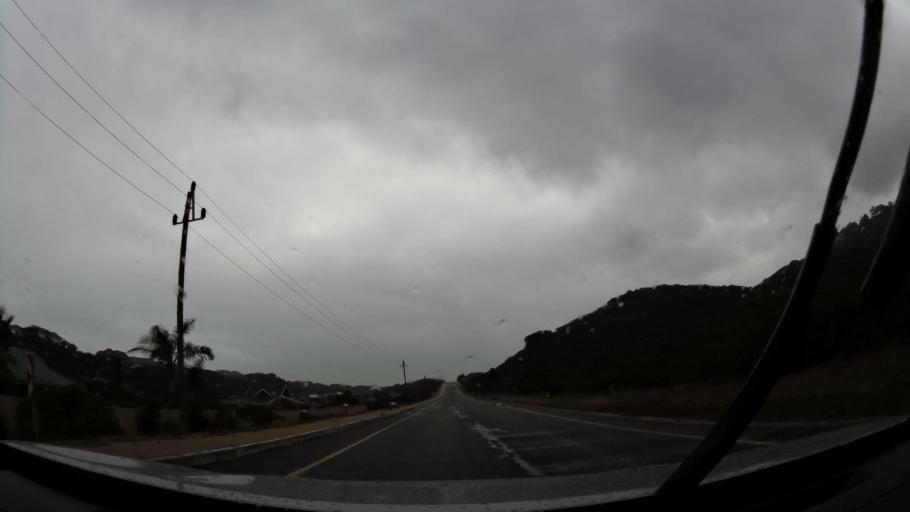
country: ZA
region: Western Cape
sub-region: Eden District Municipality
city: Mossel Bay
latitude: -34.0521
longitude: 22.2541
